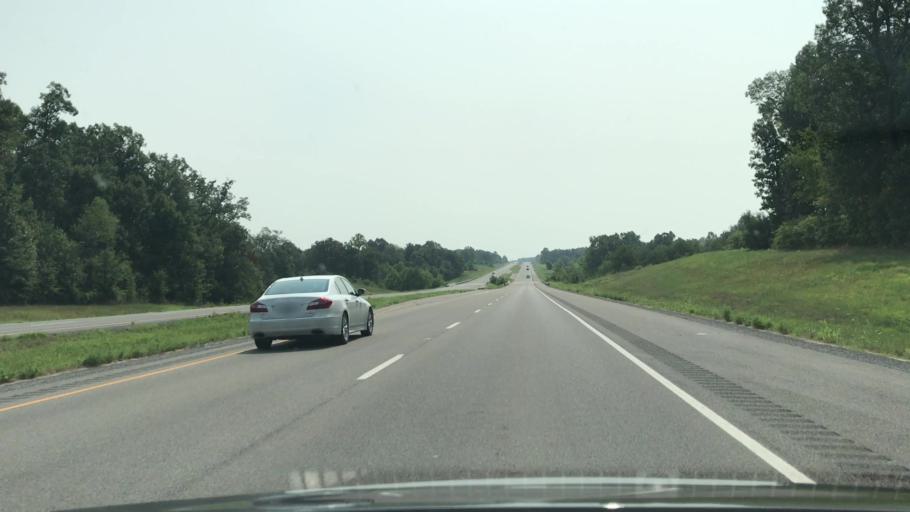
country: US
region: Kentucky
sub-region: Graves County
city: Mayfield
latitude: 36.6696
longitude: -88.4991
